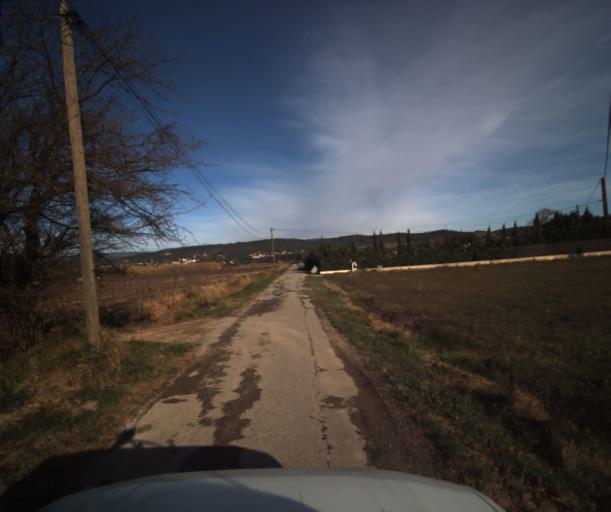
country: FR
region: Provence-Alpes-Cote d'Azur
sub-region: Departement du Vaucluse
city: Villelaure
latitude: 43.6905
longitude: 5.4482
